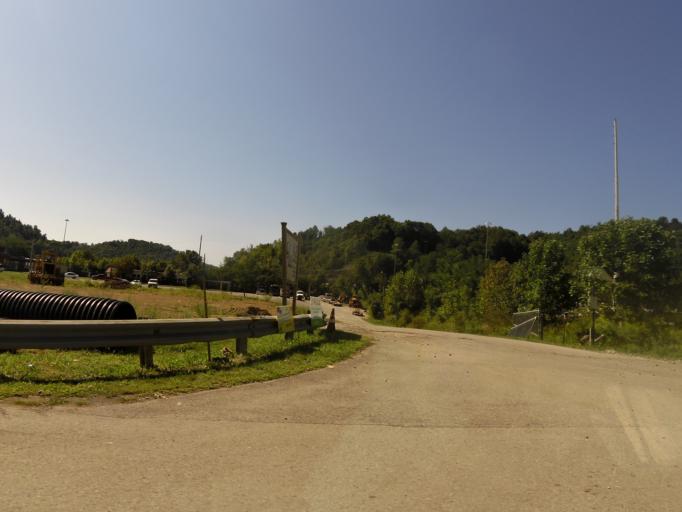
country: US
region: Kentucky
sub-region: Clay County
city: Manchester
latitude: 37.1383
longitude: -83.7673
